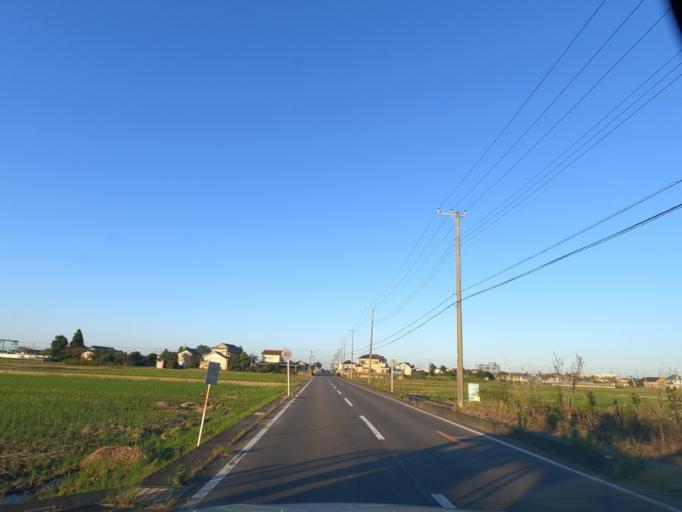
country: JP
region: Saitama
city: Kamifukuoka
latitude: 35.8888
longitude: 139.5336
